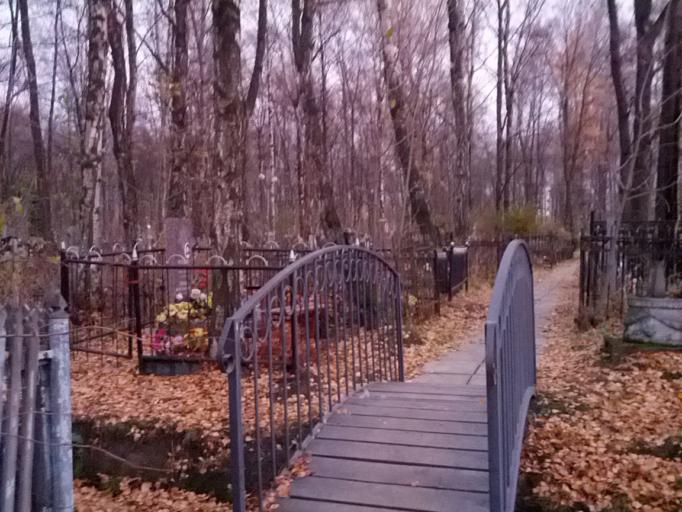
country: RU
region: St.-Petersburg
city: Obukhovo
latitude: 59.9110
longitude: 30.4286
